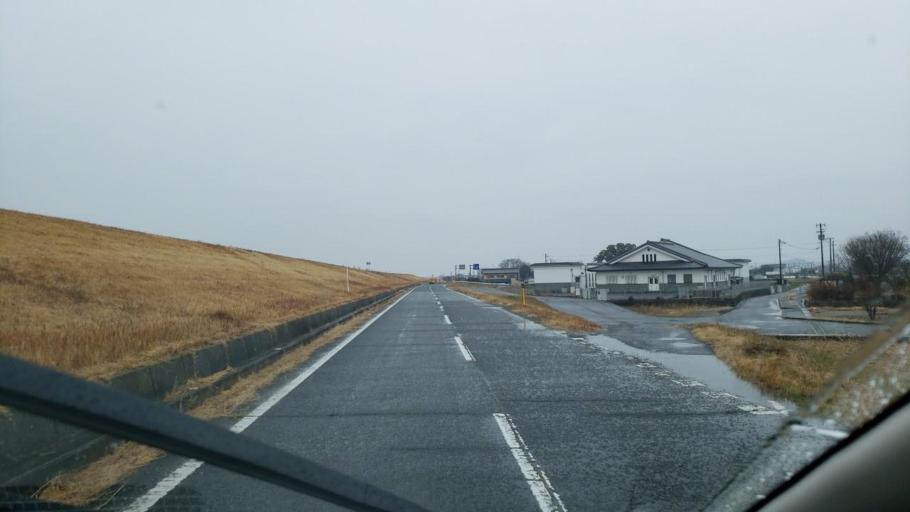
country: JP
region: Tokushima
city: Kamojimacho-jogejima
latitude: 34.0693
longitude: 134.3233
